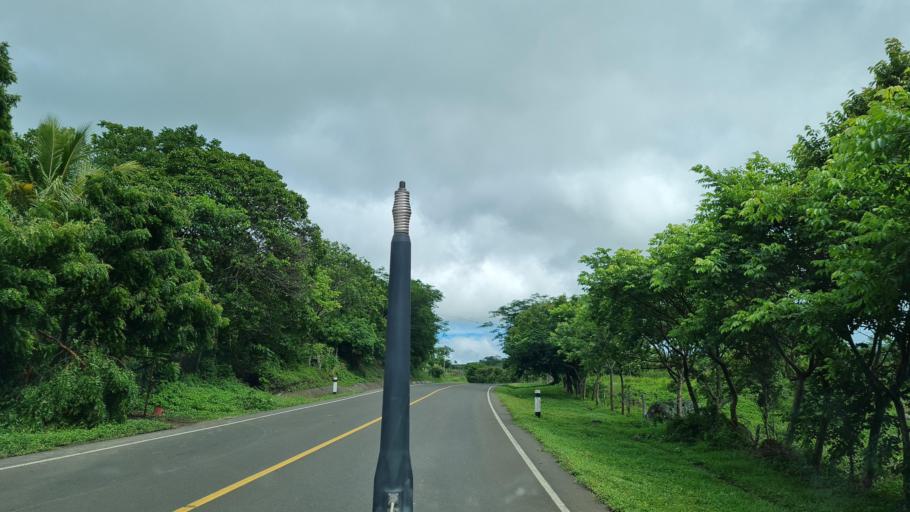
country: NI
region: Matagalpa
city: Terrabona
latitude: 12.5920
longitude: -85.9492
